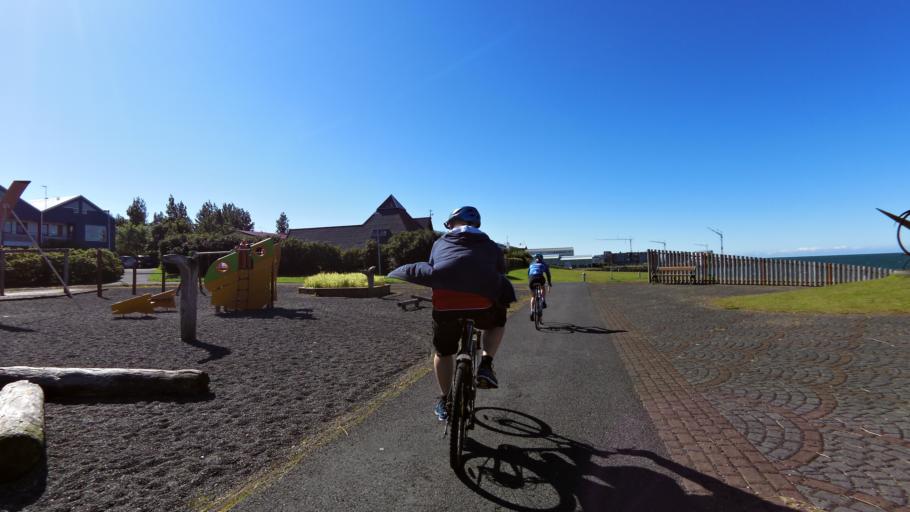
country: IS
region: Capital Region
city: Kopavogur
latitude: 64.1156
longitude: -21.9135
